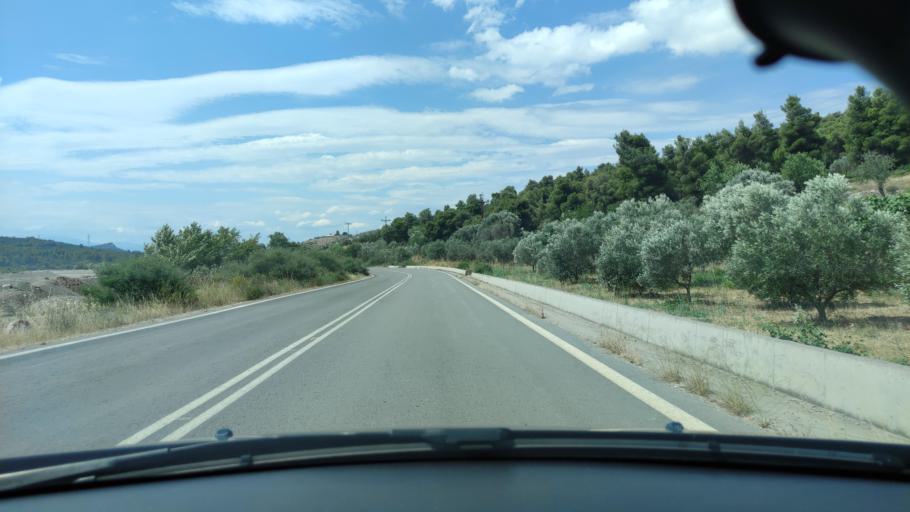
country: GR
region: Central Greece
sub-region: Nomos Evvoias
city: Afration
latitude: 38.4833
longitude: 23.6883
